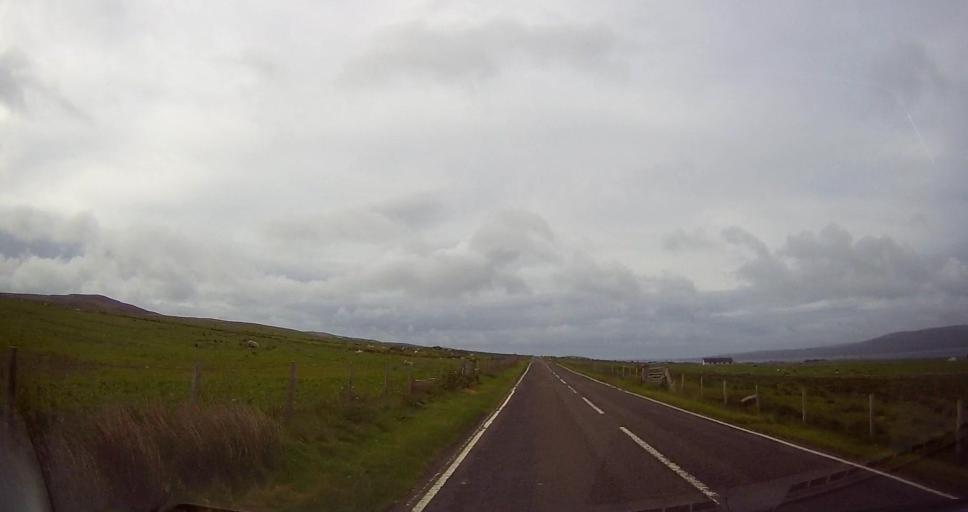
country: GB
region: Scotland
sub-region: Orkney Islands
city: Stromness
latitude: 58.9522
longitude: -3.2178
